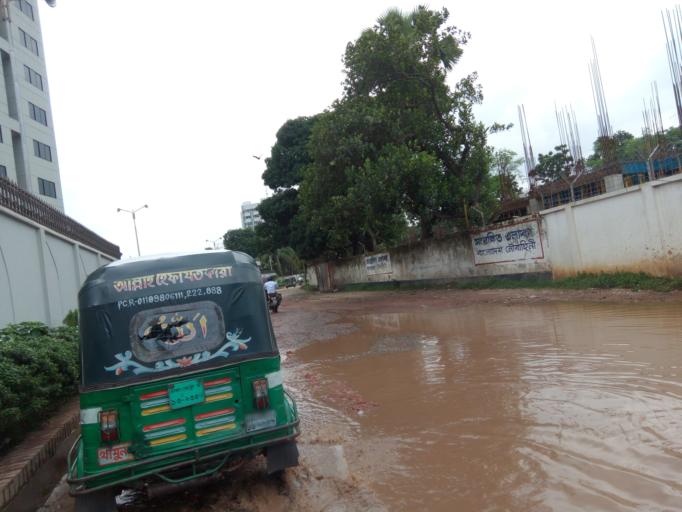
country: BD
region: Dhaka
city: Paltan
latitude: 23.7728
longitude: 90.3926
